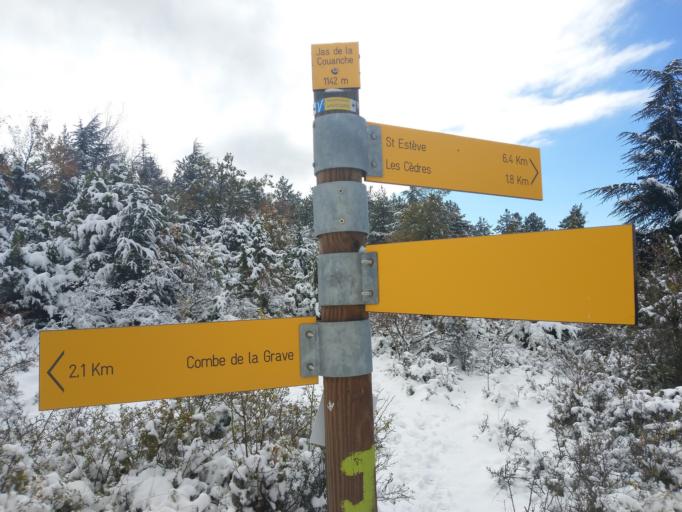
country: FR
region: Provence-Alpes-Cote d'Azur
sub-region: Departement du Vaucluse
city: Bedoin
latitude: 44.1468
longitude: 5.2694
